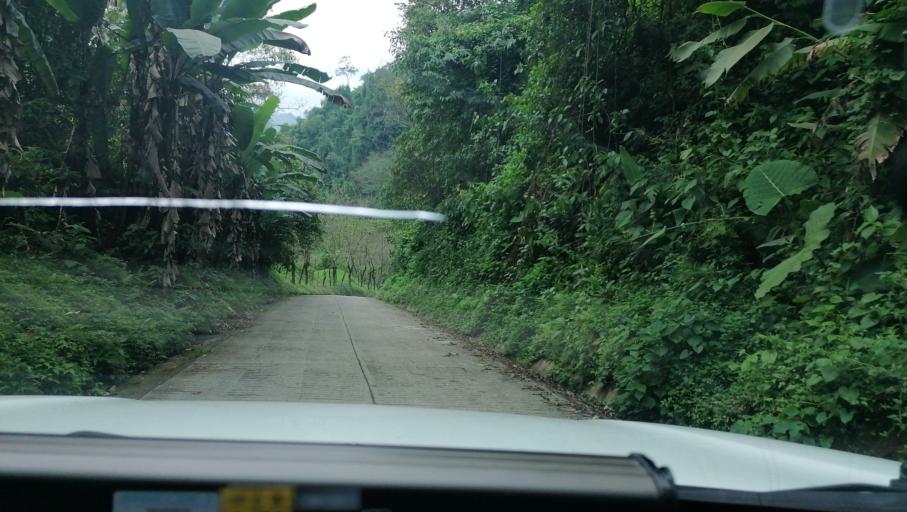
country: MX
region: Chiapas
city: Ixtacomitan
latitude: 17.3404
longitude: -93.1204
